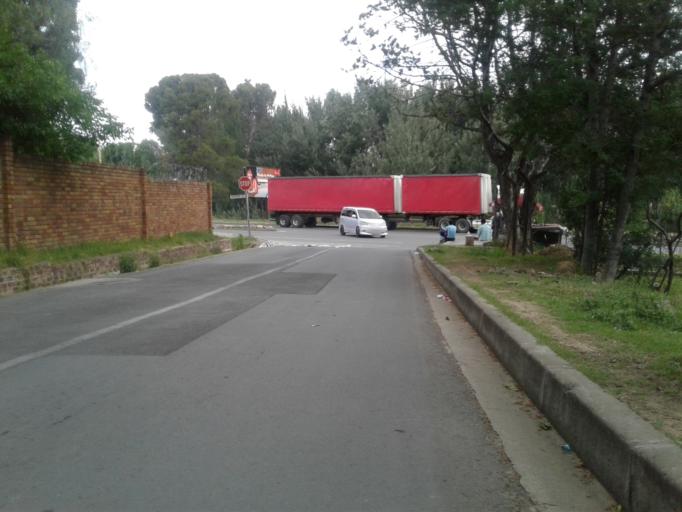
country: LS
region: Maseru
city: Maseru
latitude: -29.3098
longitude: 27.4755
